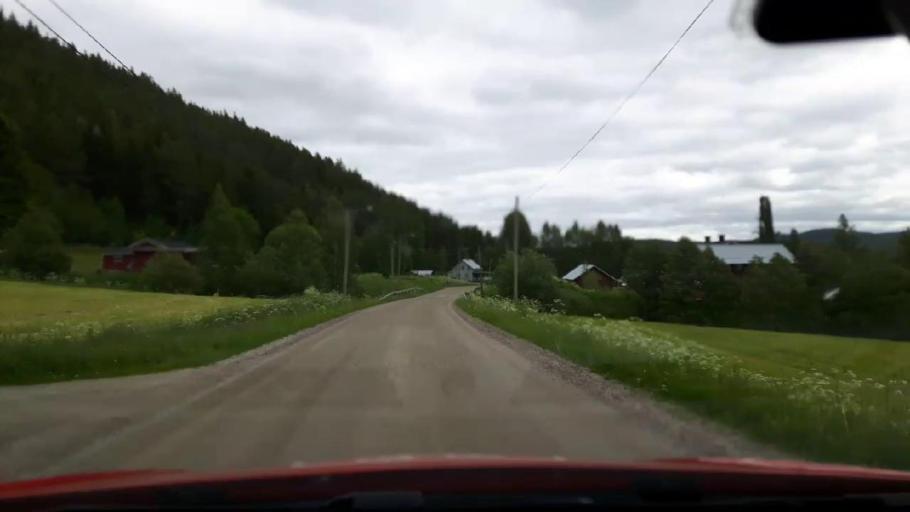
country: SE
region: Jaemtland
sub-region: Ragunda Kommun
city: Hammarstrand
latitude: 63.1725
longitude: 16.2033
